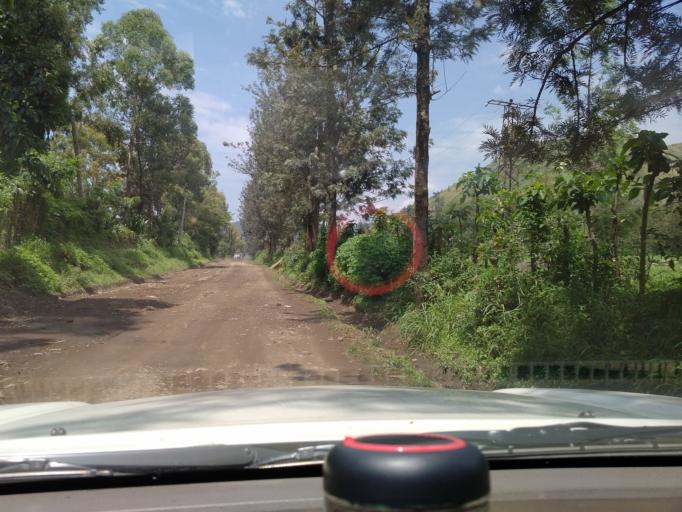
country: CD
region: Nord Kivu
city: Sake
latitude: -1.6047
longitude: 29.0360
